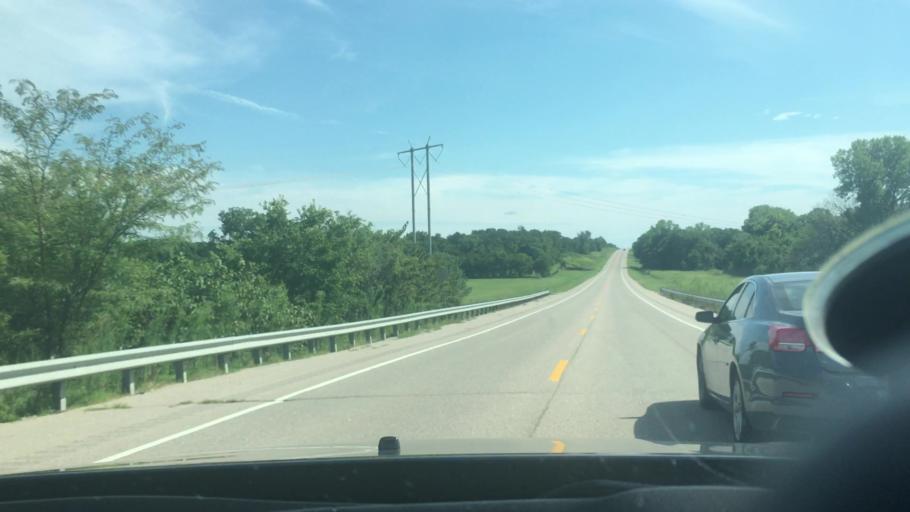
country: US
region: Oklahoma
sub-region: Seminole County
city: Konawa
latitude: 35.0290
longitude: -96.6782
